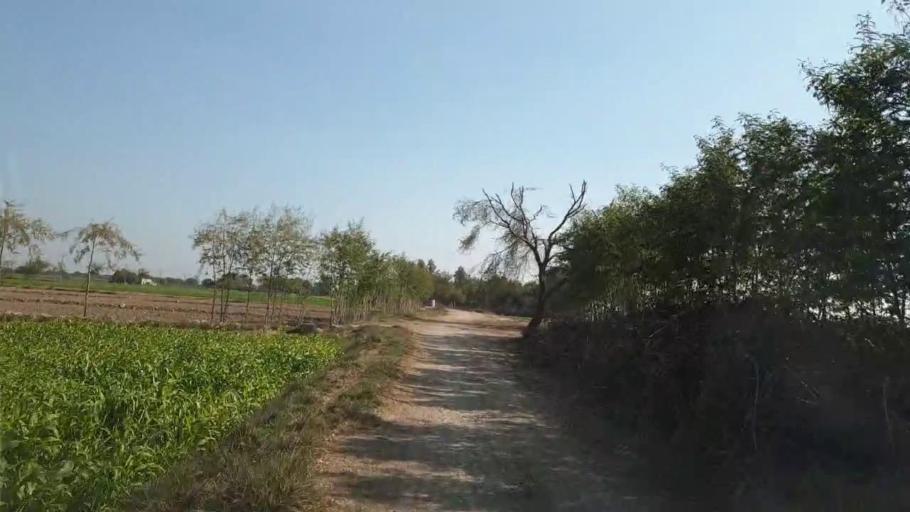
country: PK
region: Sindh
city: Tando Jam
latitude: 25.5038
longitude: 68.4769
